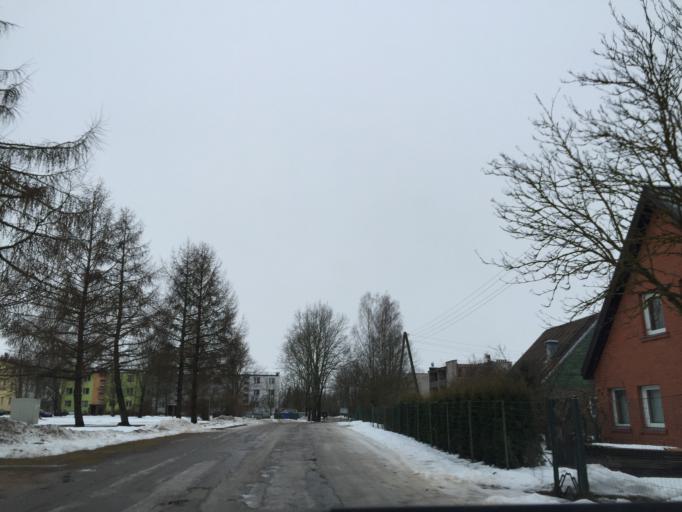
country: LV
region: Krimulda
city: Ragana
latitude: 57.1826
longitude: 24.7024
